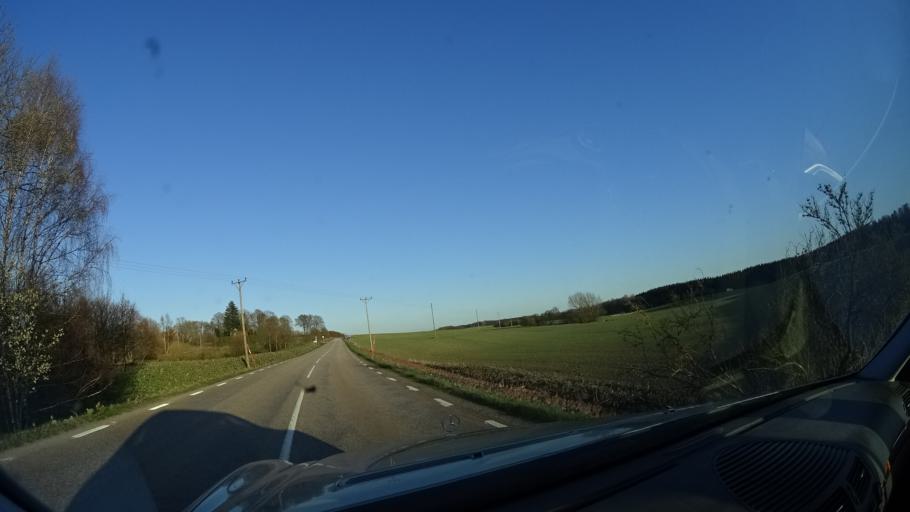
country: SE
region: Skane
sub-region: Klippans Kommun
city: Ljungbyhed
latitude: 55.9791
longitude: 13.1938
